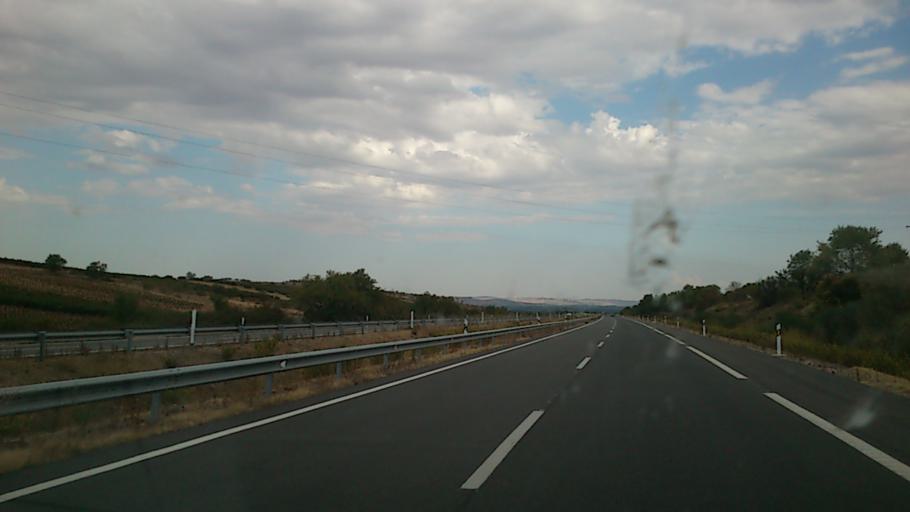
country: ES
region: La Rioja
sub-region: Provincia de La Rioja
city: Alcanadre
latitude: 42.3804
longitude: -2.1087
